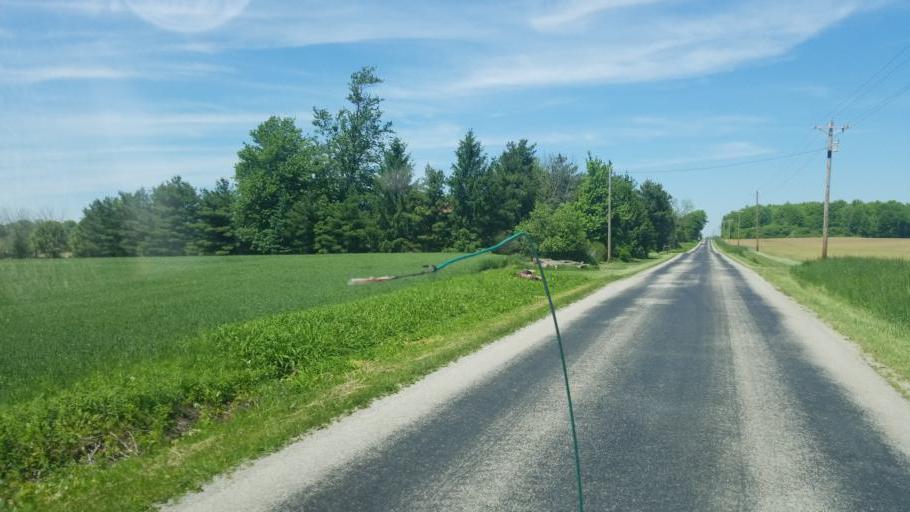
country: US
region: Ohio
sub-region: Huron County
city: Greenwich
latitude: 41.1265
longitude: -82.5384
